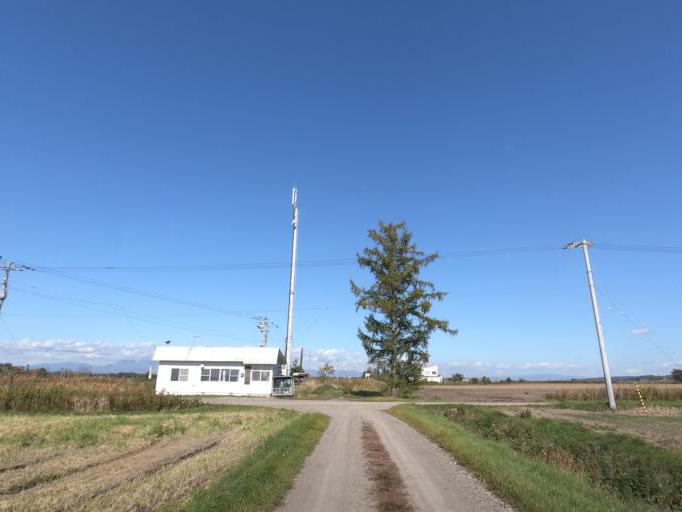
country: JP
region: Hokkaido
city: Otofuke
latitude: 43.0372
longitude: 143.2723
